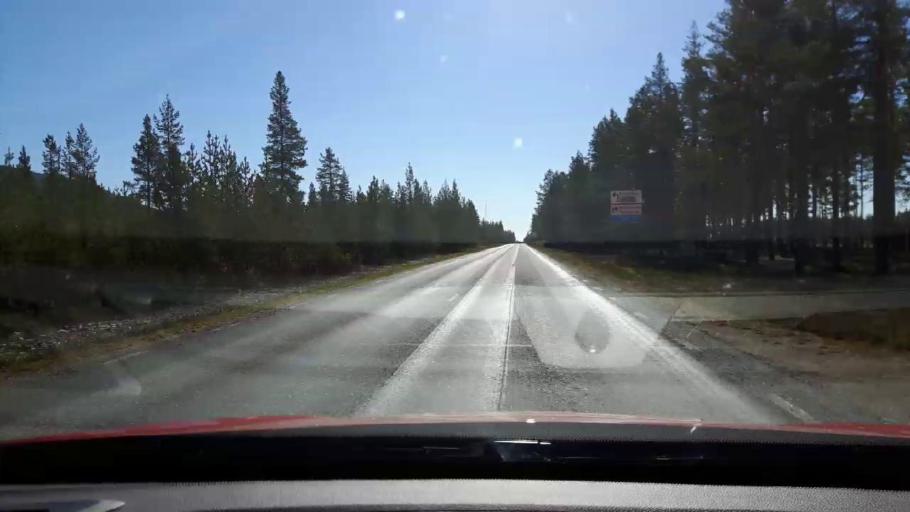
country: SE
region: Jaemtland
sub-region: Harjedalens Kommun
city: Sveg
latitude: 62.4143
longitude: 13.9159
